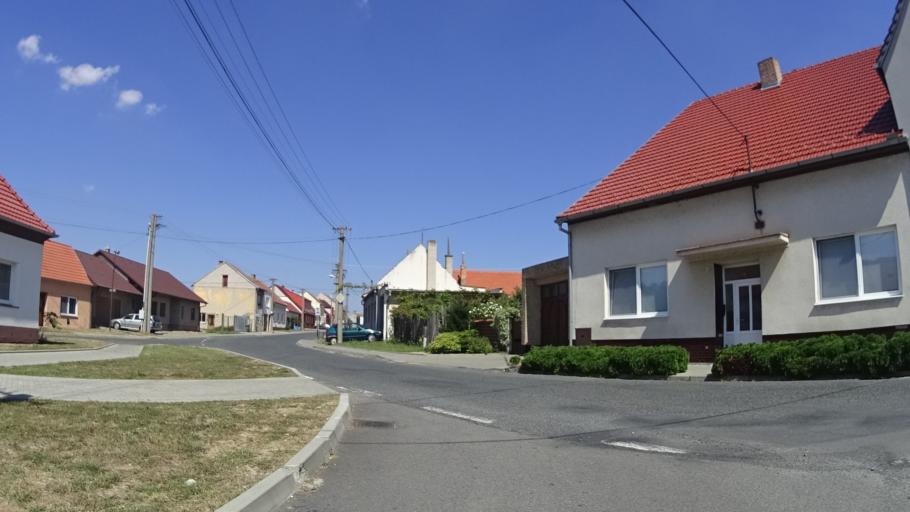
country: CZ
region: South Moravian
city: Vnorovy
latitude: 48.9229
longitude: 17.3391
